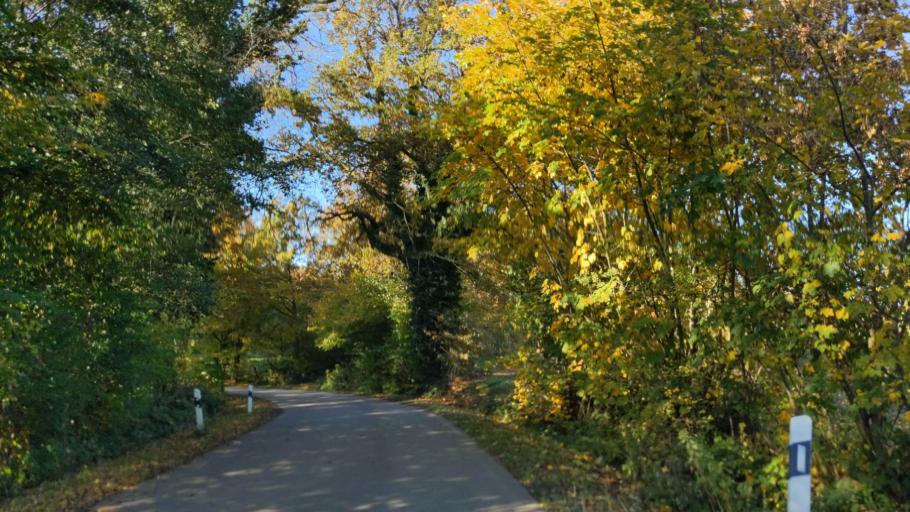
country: DE
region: Schleswig-Holstein
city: Kasseedorf
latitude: 54.1351
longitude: 10.7276
